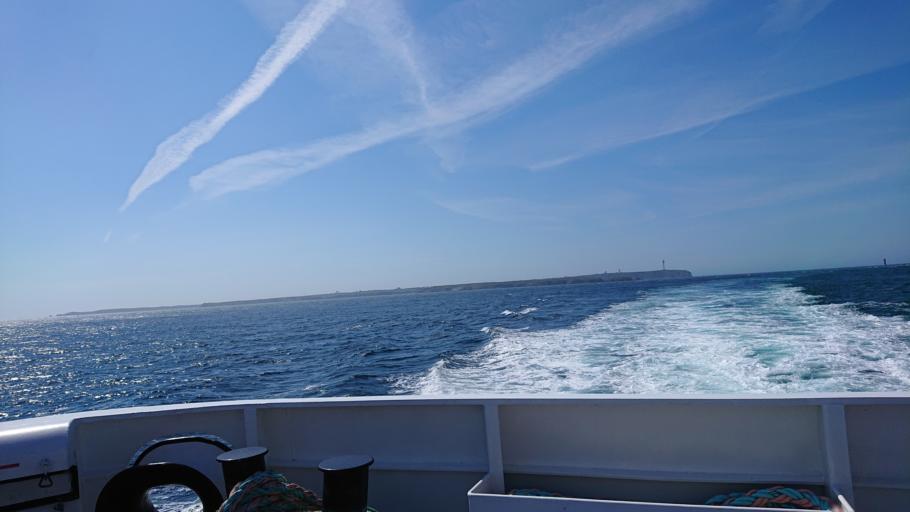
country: FR
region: Brittany
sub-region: Departement du Finistere
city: Porspoder
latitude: 48.4498
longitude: -5.0051
